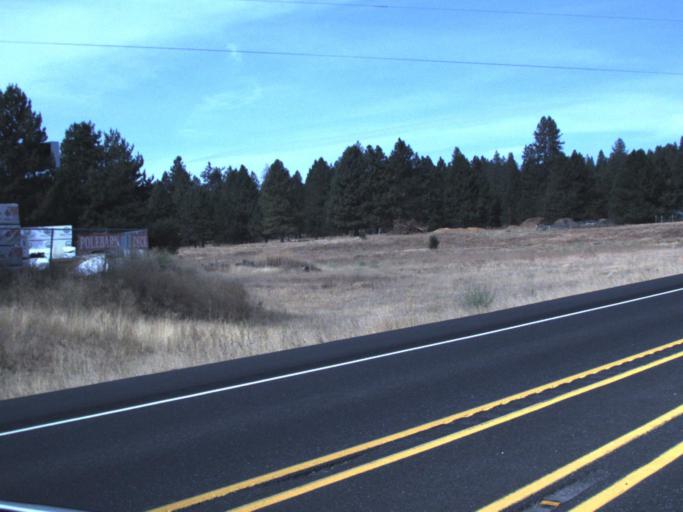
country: US
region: Washington
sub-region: Spokane County
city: Deer Park
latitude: 47.9191
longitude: -117.4546
